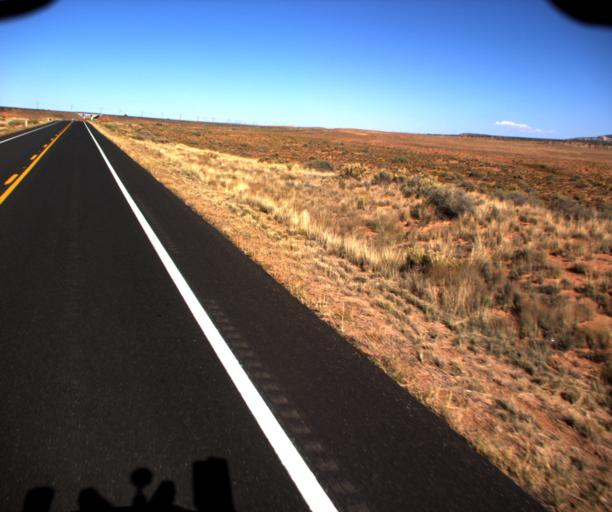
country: US
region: Arizona
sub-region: Coconino County
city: Kaibito
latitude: 36.3871
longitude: -110.8832
